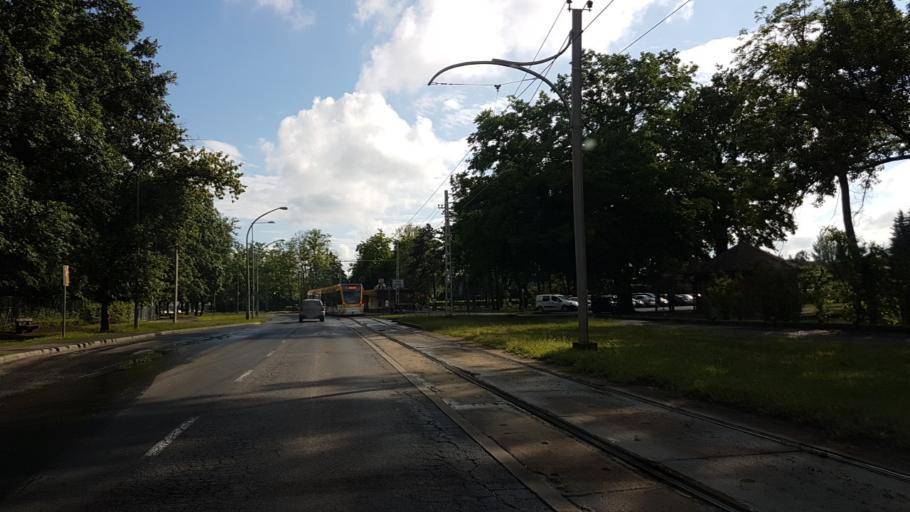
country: HU
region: Hajdu-Bihar
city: Debrecen
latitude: 47.5537
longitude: 21.6239
